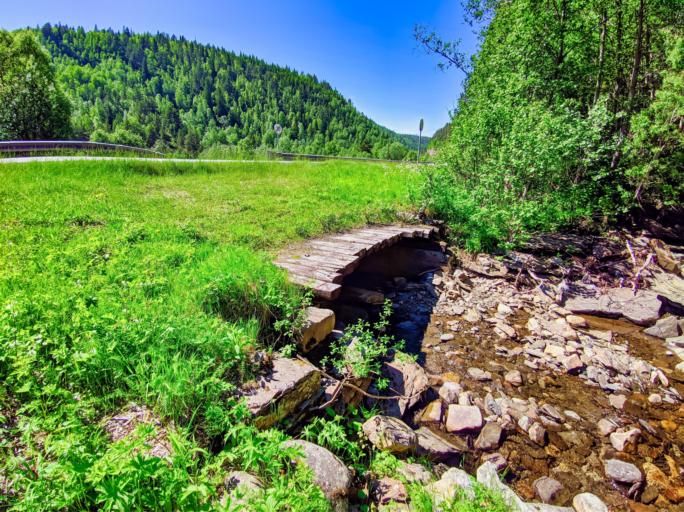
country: NO
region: Sor-Trondelag
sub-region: Rennebu
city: Berkak
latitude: 62.7020
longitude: 10.1303
